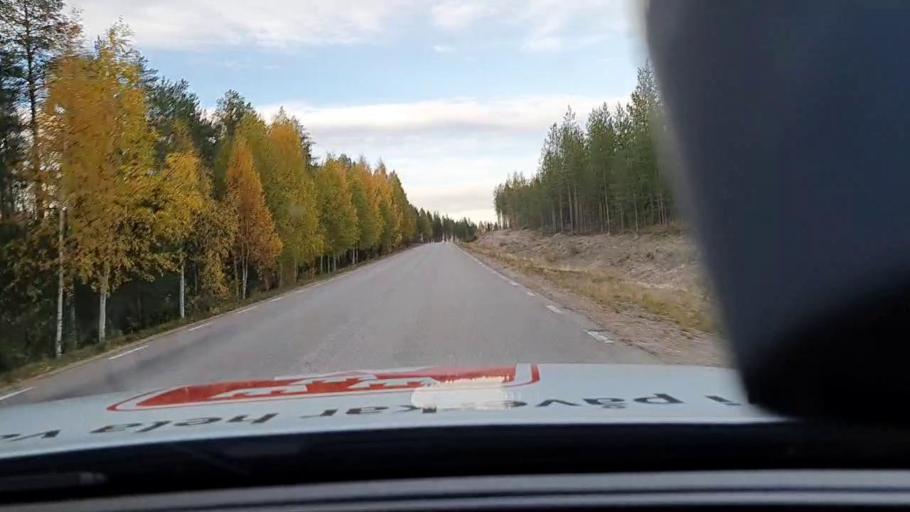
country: SE
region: Norrbotten
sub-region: Overkalix Kommun
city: OEverkalix
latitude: 66.3272
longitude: 22.7722
